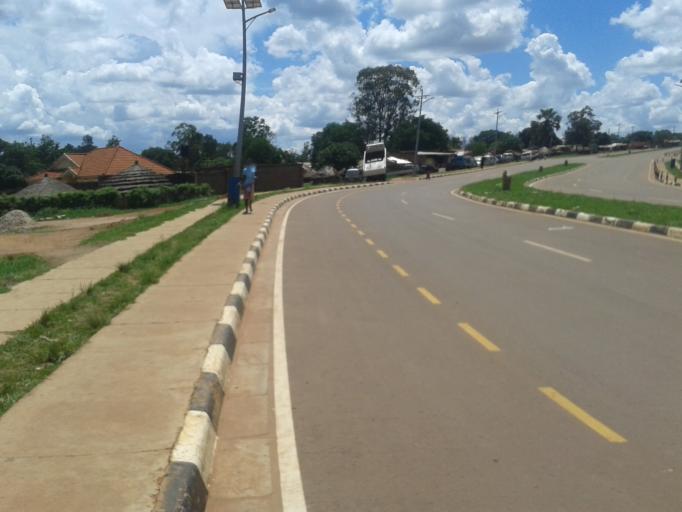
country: UG
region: Northern Region
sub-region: Gulu District
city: Gulu
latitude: 2.7642
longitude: 32.2937
